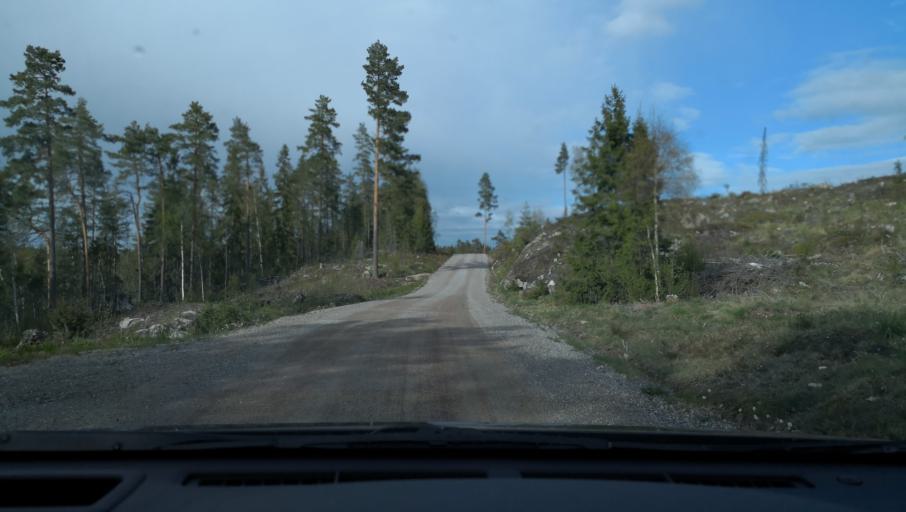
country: SE
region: Vaestmanland
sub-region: Fagersta Kommun
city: Fagersta
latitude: 60.1602
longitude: 15.7157
